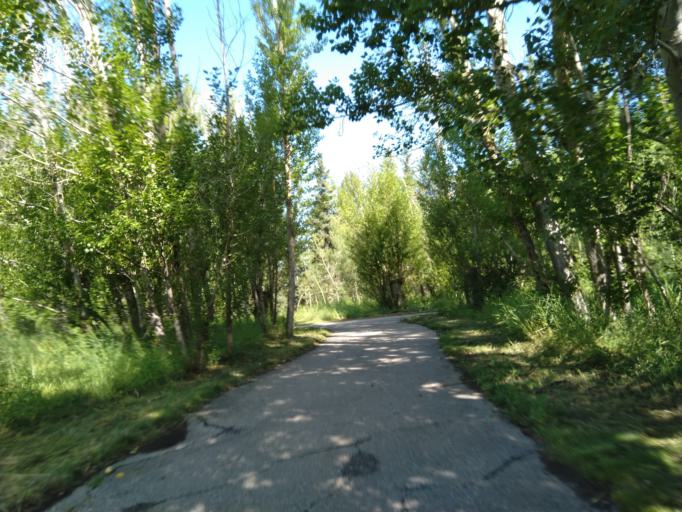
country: CA
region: Alberta
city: Calgary
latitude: 51.0956
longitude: -114.2399
